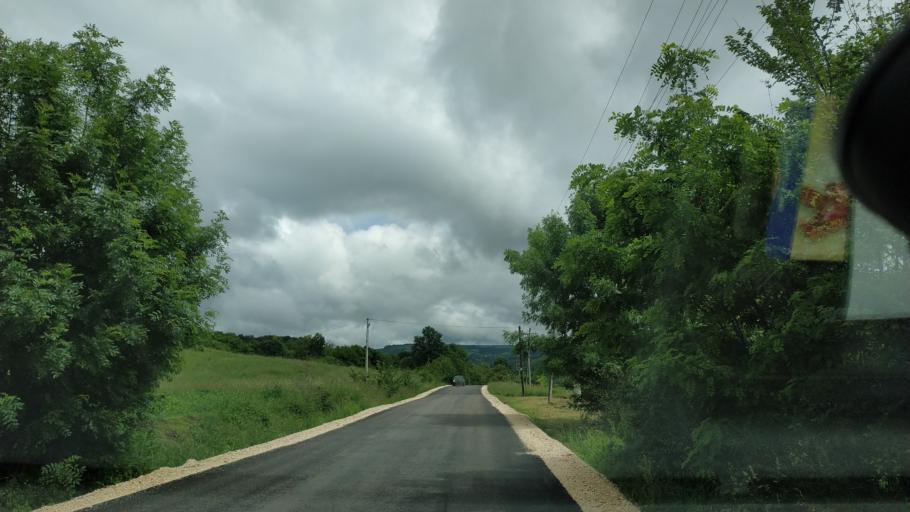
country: RS
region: Central Serbia
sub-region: Zajecarski Okrug
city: Soko Banja
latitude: 43.6510
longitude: 21.9015
